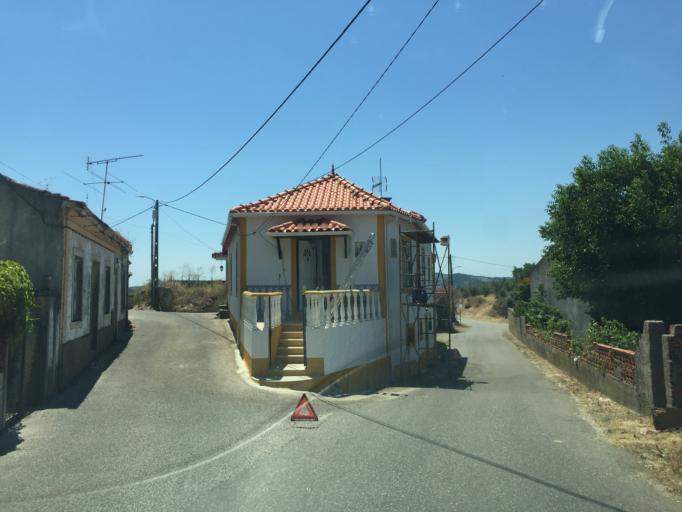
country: PT
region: Santarem
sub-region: Constancia
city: Constancia
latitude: 39.5727
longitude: -8.2937
